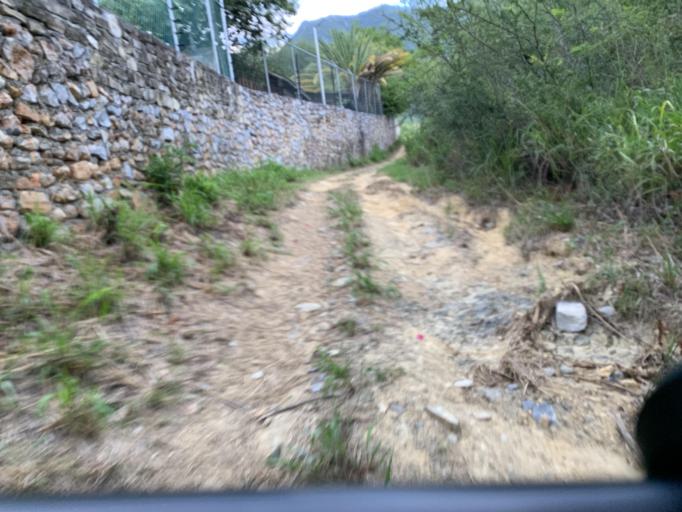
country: MX
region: Nuevo Leon
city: Santiago
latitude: 25.5054
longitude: -100.1823
